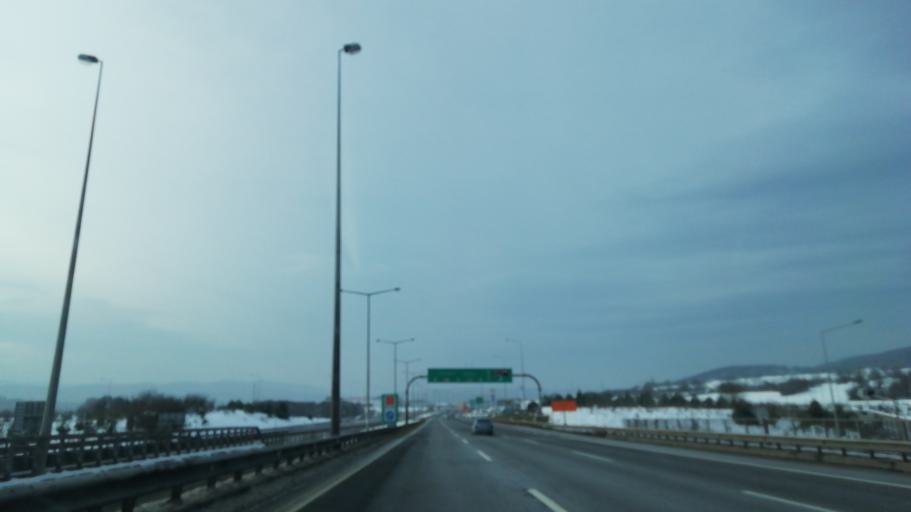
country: TR
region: Bolu
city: Bolu
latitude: 40.7217
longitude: 31.4790
